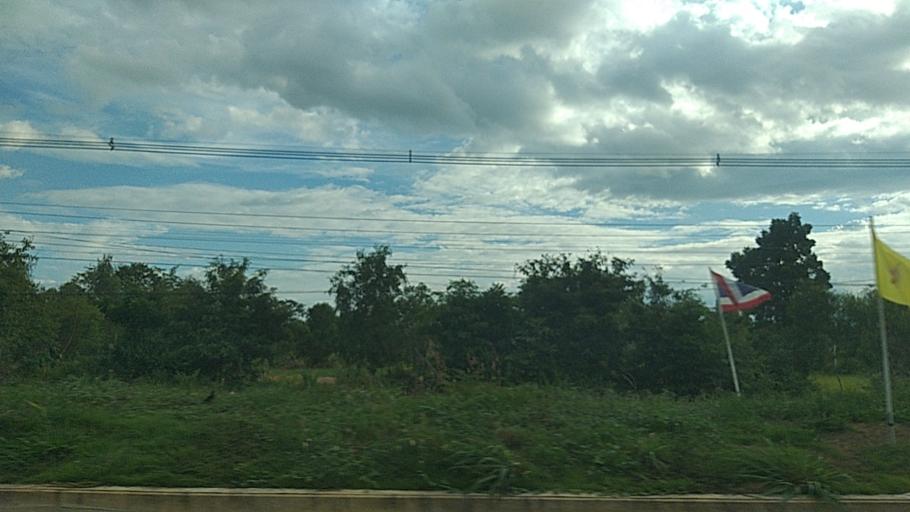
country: TH
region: Surin
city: Kap Choeng
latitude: 14.5543
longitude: 103.5056
